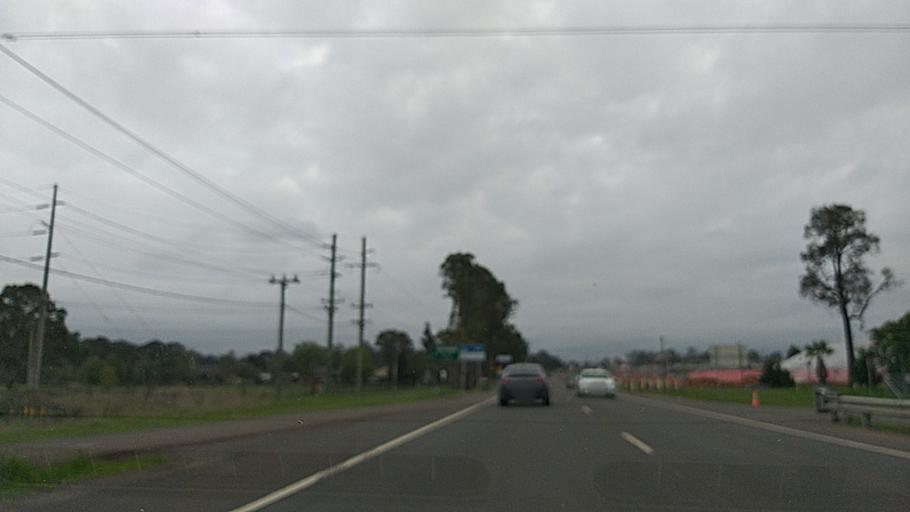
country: AU
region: New South Wales
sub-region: Penrith Municipality
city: Glenmore Park
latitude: -33.7972
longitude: 150.6983
